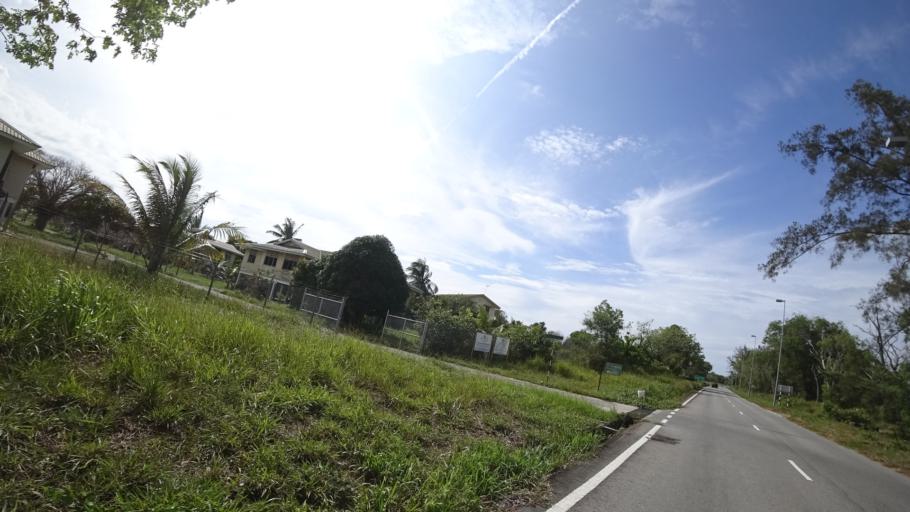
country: BN
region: Tutong
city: Tutong
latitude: 4.8202
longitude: 114.6629
